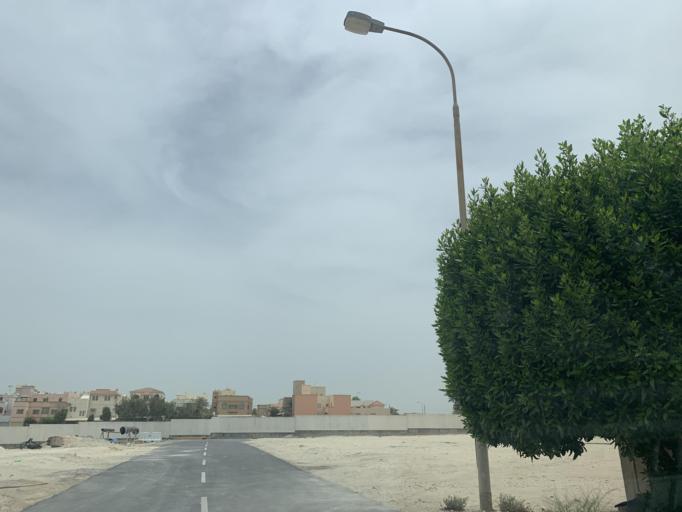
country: BH
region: Northern
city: Ar Rifa'
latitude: 26.1394
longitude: 50.5538
